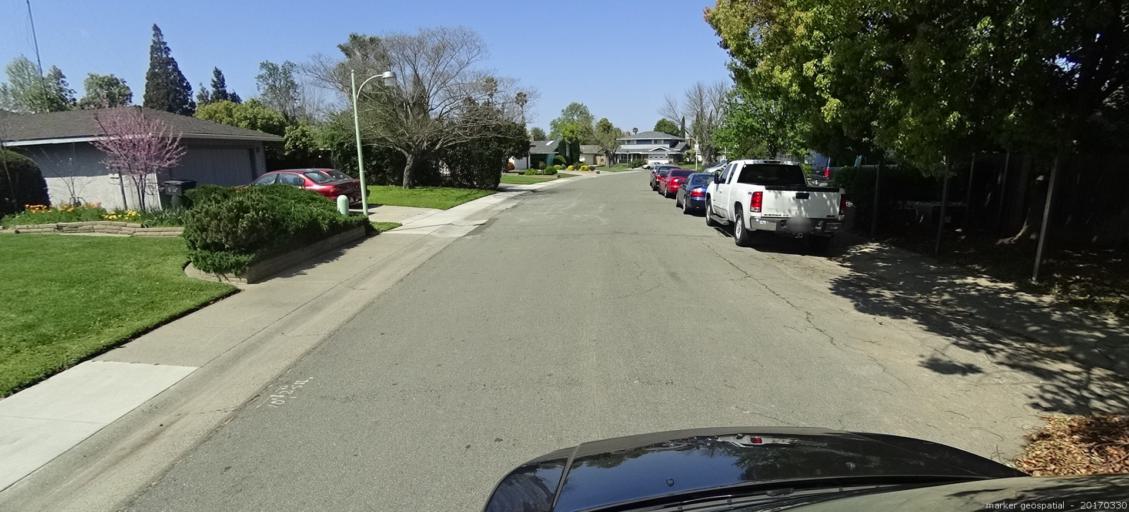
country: US
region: California
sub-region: Sacramento County
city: Florin
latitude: 38.4650
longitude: -121.4292
